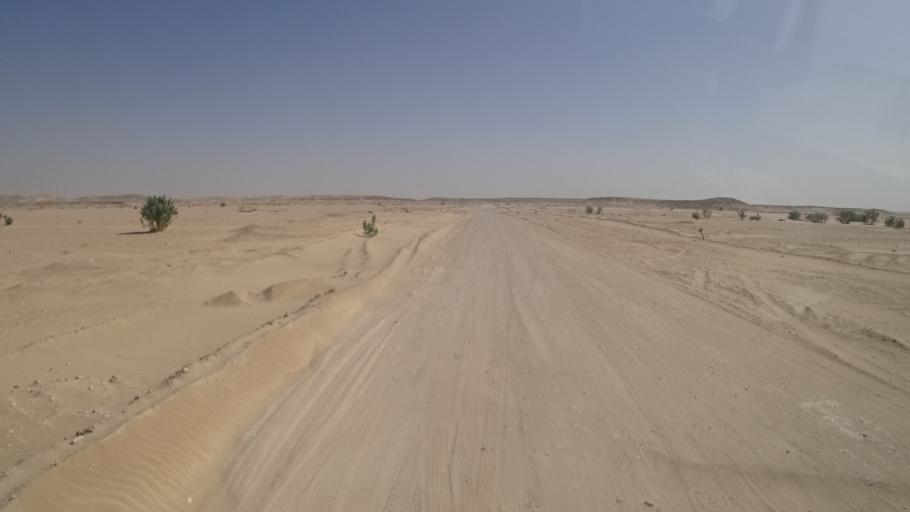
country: YE
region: Al Mahrah
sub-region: Shahan
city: Shihan as Sufla
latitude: 17.8762
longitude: 52.6057
